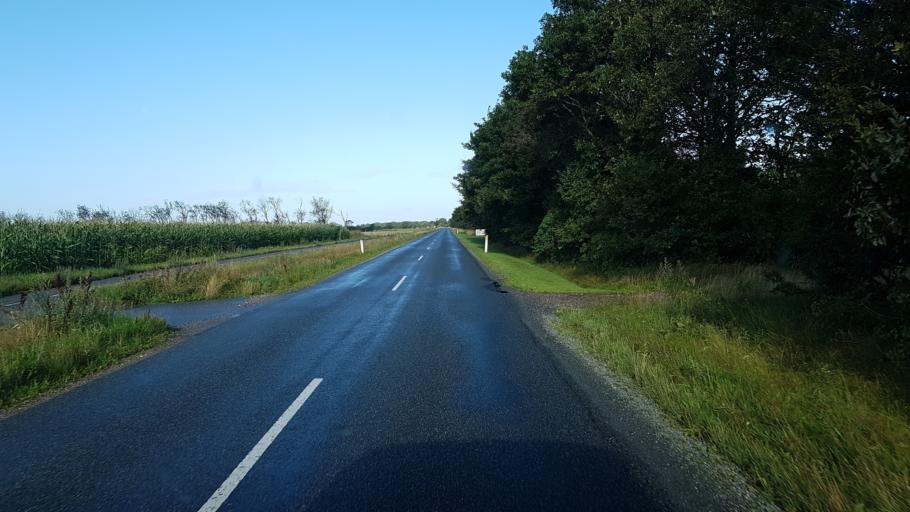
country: DK
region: South Denmark
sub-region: Esbjerg Kommune
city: Bramming
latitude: 55.4838
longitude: 8.7273
